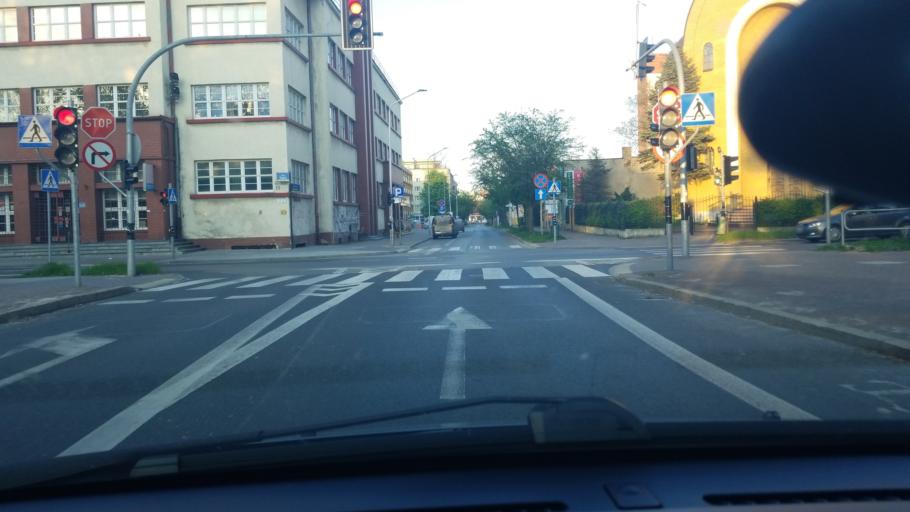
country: PL
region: Silesian Voivodeship
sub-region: Czestochowa
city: Czestochowa
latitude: 50.8087
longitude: 19.1134
